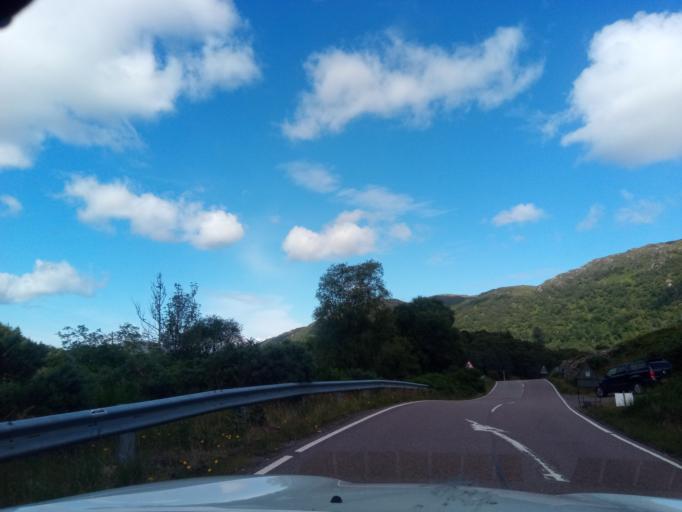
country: GB
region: Scotland
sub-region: Argyll and Bute
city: Isle Of Mull
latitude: 56.7809
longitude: -5.7461
